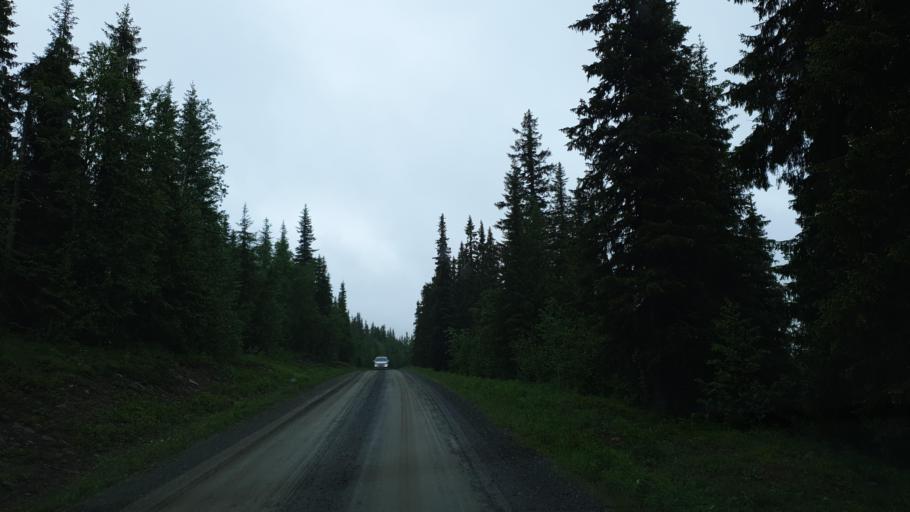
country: SE
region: Vaesterbotten
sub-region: Vilhelmina Kommun
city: Sjoberg
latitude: 65.3304
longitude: 15.9102
